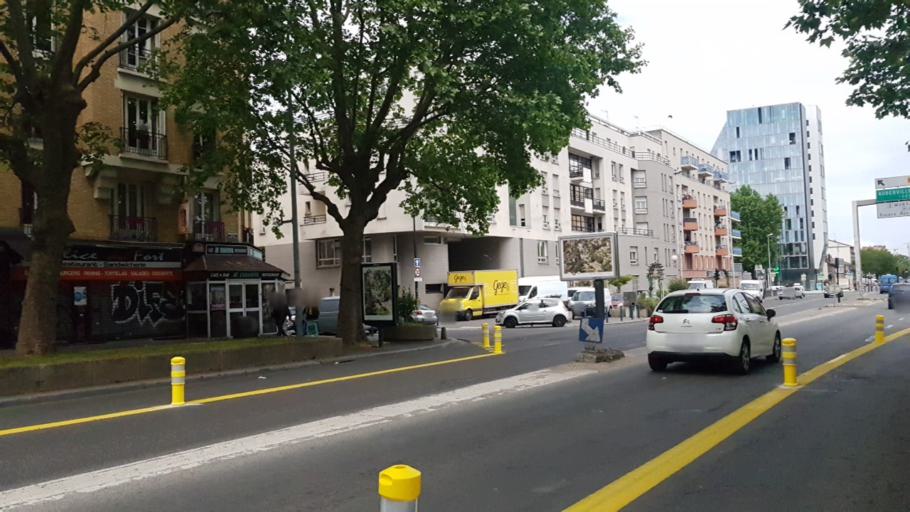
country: FR
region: Ile-de-France
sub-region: Departement de Seine-Saint-Denis
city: La Courneuve
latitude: 48.9137
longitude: 2.4030
